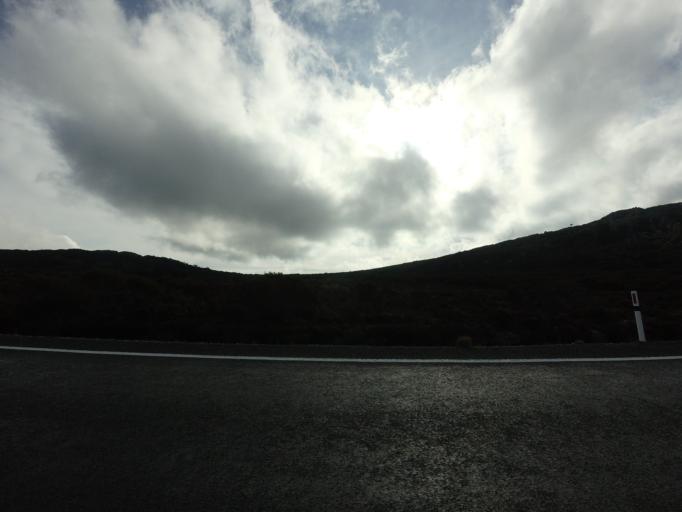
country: AU
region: Tasmania
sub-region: Meander Valley
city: Deloraine
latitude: -41.7307
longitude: 146.7092
